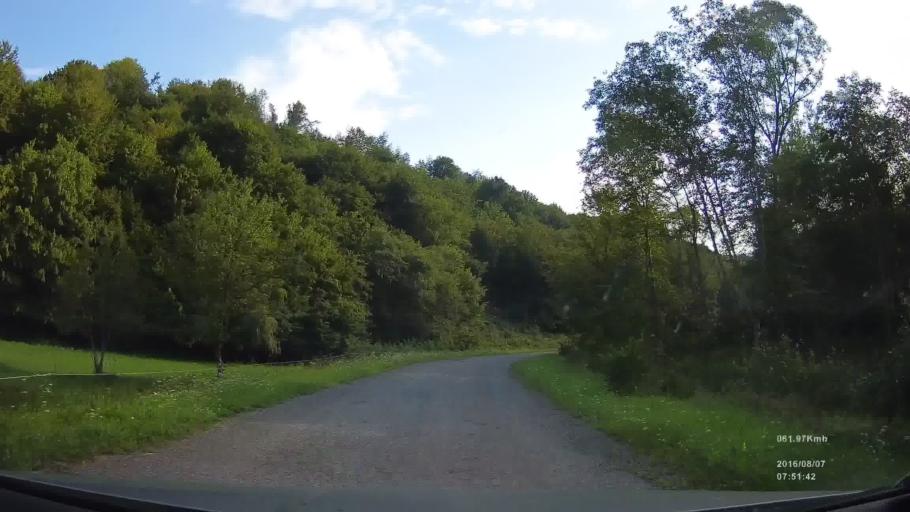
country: SK
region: Presovsky
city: Medzilaborce
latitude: 49.3060
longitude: 21.7890
